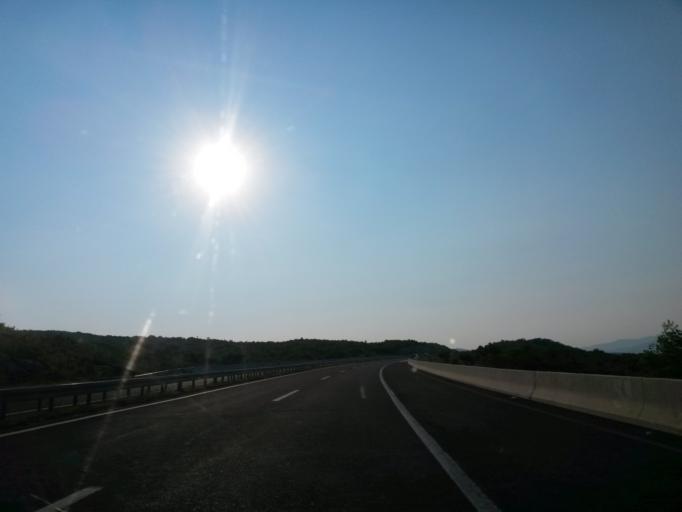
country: HR
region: Splitsko-Dalmatinska
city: Dugopolje
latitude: 43.5828
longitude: 16.6463
